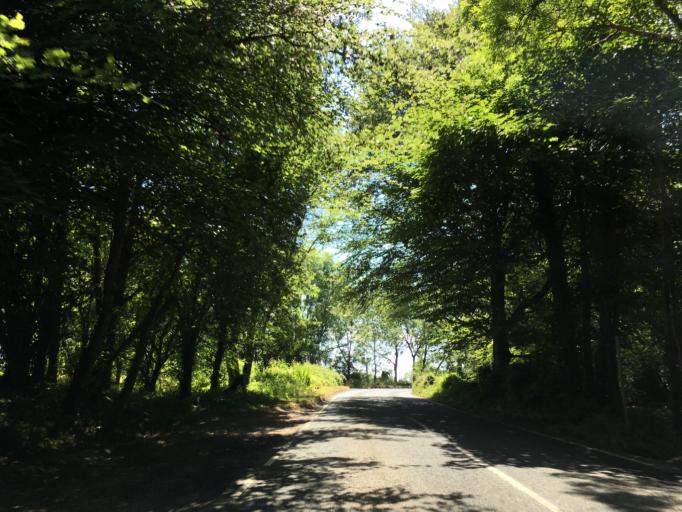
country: GB
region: England
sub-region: Gloucestershire
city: Painswick
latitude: 51.7796
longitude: -2.2269
